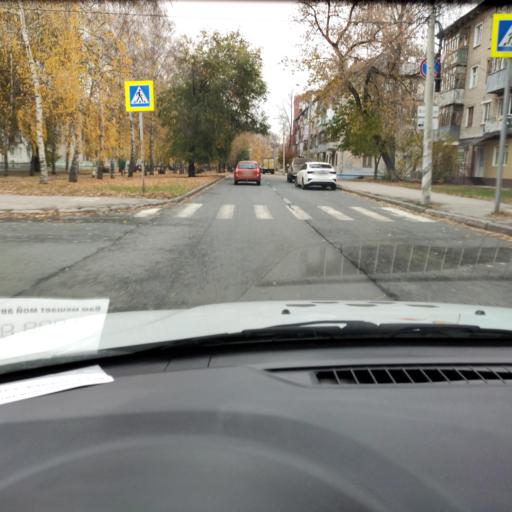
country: RU
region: Samara
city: Tol'yatti
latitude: 53.5150
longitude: 49.4129
